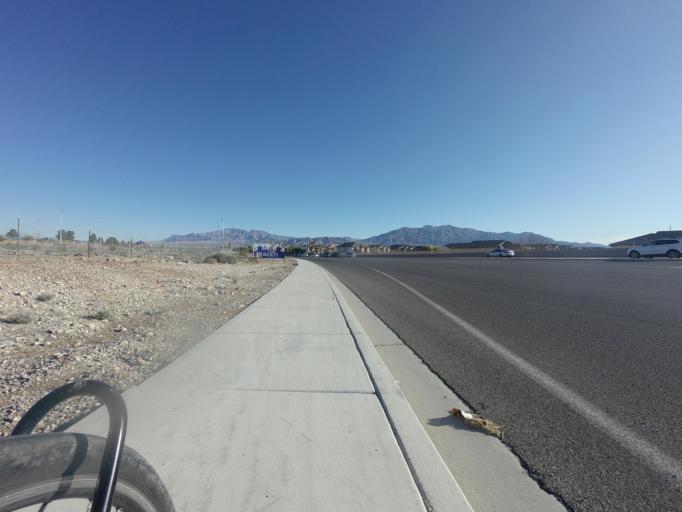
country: US
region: Nevada
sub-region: Clark County
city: Summerlin South
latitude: 36.3161
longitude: -115.2974
